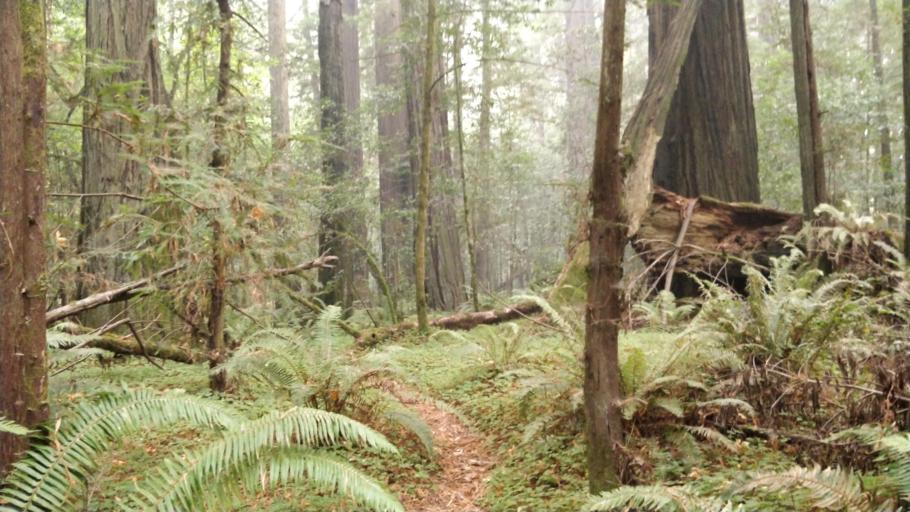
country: US
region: California
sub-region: Humboldt County
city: Rio Dell
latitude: 40.4176
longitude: -123.9685
